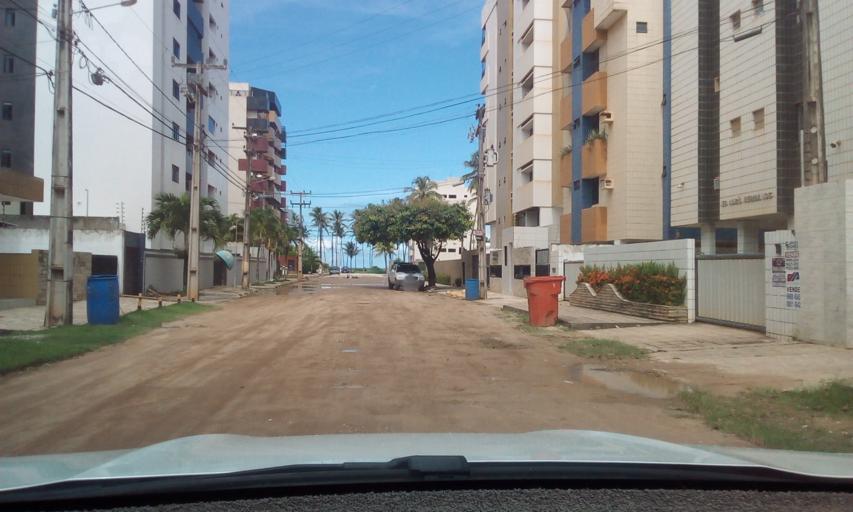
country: BR
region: Paraiba
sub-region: Cabedelo
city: Cabedelo
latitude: -7.0372
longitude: -34.8398
